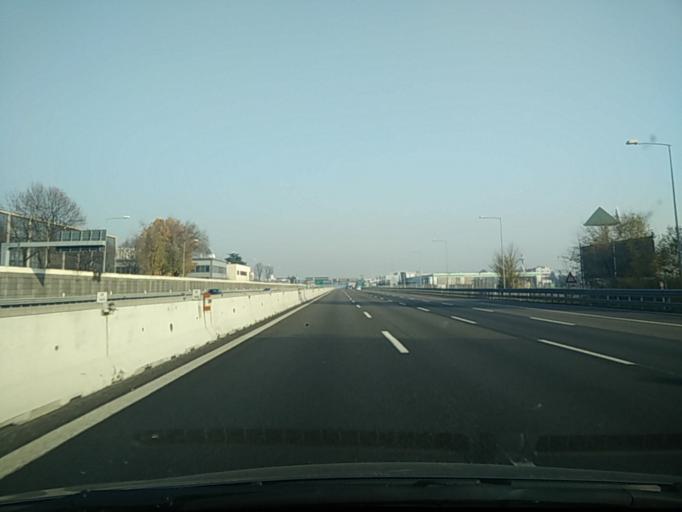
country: IT
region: Lombardy
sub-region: Provincia di Monza e Brianza
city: Caponago
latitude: 45.5700
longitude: 9.3622
